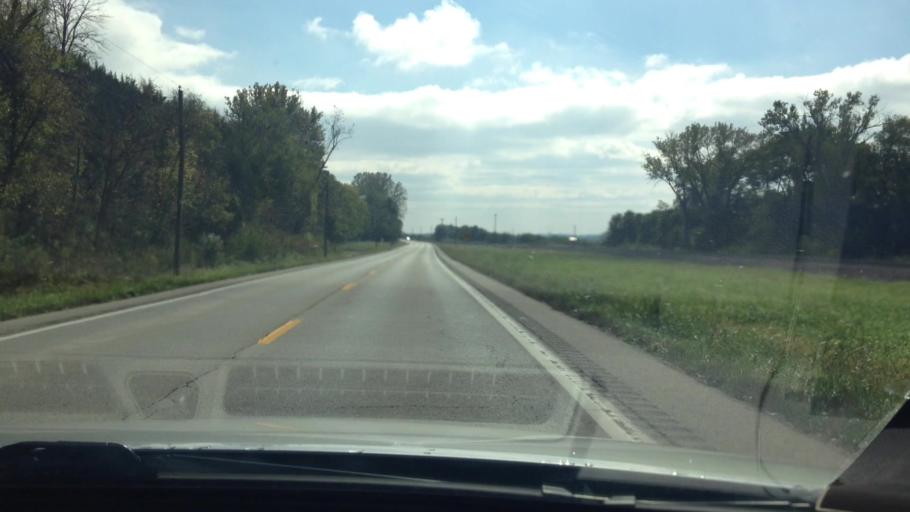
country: US
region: Kansas
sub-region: Leavenworth County
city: Leavenworth
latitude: 39.3059
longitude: -94.8485
